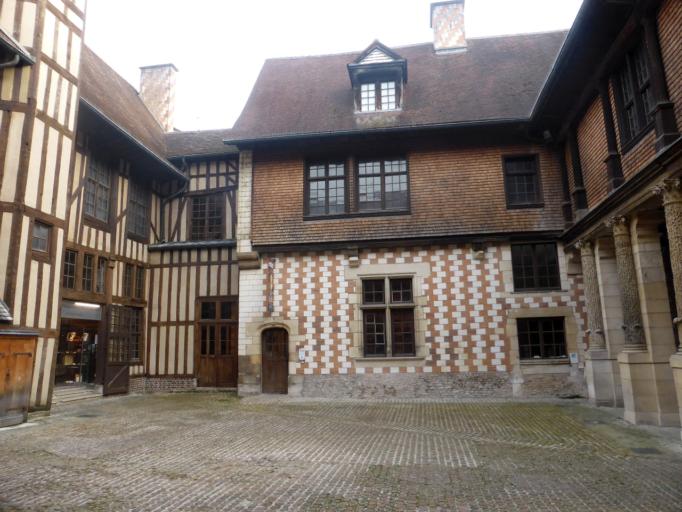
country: FR
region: Champagne-Ardenne
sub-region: Departement de l'Aube
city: Troyes
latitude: 48.2943
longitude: 4.0731
